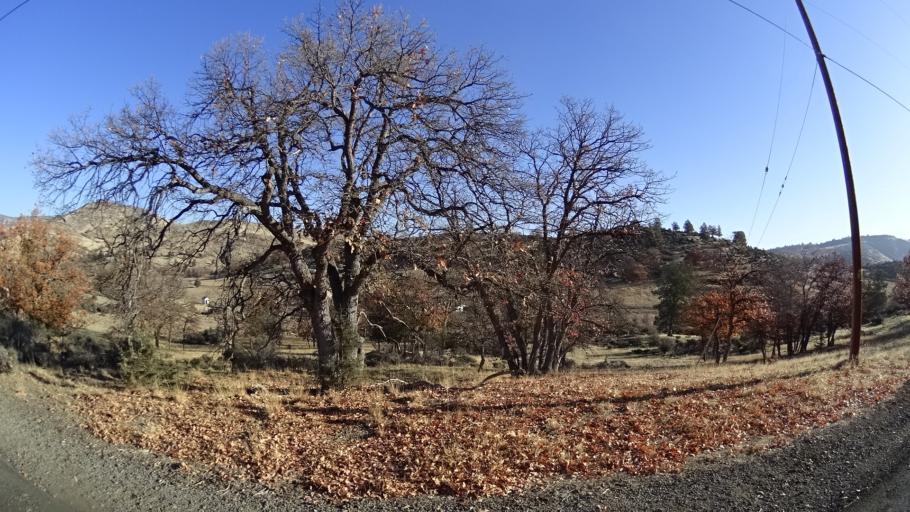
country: US
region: California
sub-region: Siskiyou County
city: Montague
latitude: 41.8923
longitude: -122.4947
